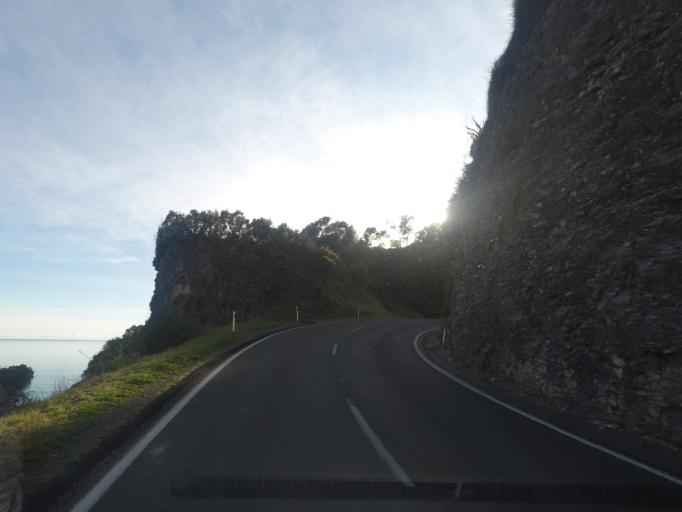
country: NZ
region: Tasman
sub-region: Tasman District
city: Takaka
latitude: -40.8218
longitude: 172.9011
